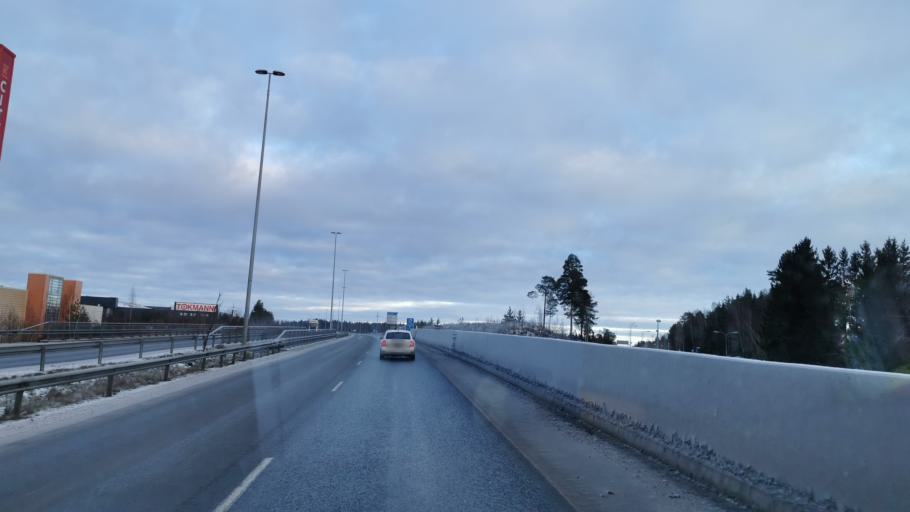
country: FI
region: Ostrobothnia
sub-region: Vaasa
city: Korsholm
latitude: 63.1106
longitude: 21.6640
